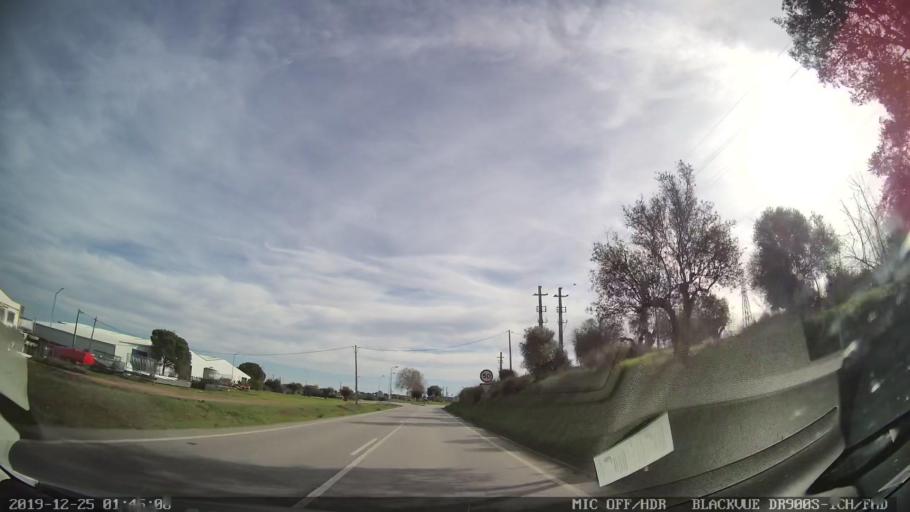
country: PT
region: Portalegre
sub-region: Arronches
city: Arronches
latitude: 39.1158
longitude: -7.2886
